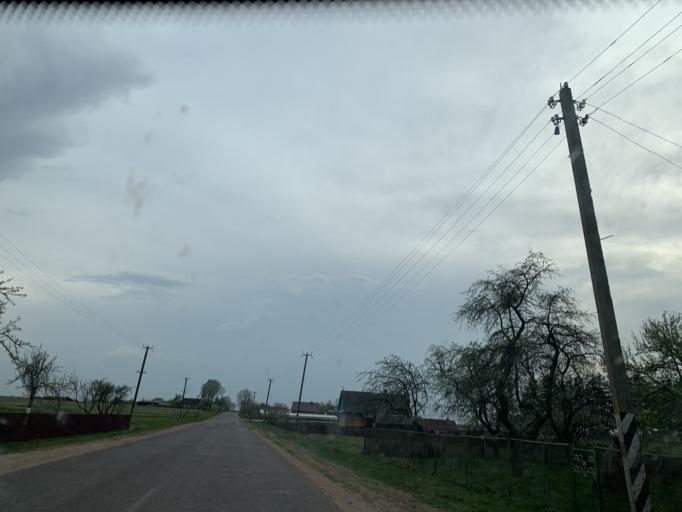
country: BY
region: Minsk
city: Kapyl'
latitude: 53.2786
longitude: 26.9743
